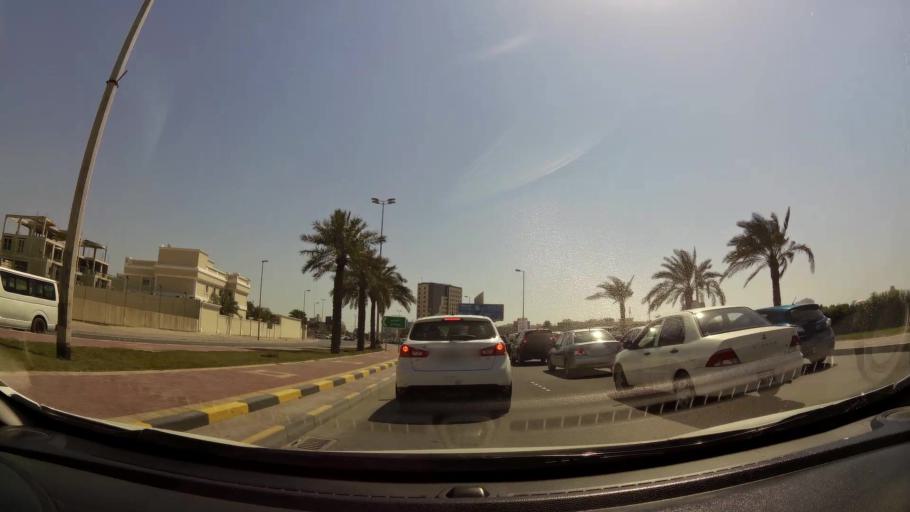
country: BH
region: Manama
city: Manama
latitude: 26.2105
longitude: 50.5970
